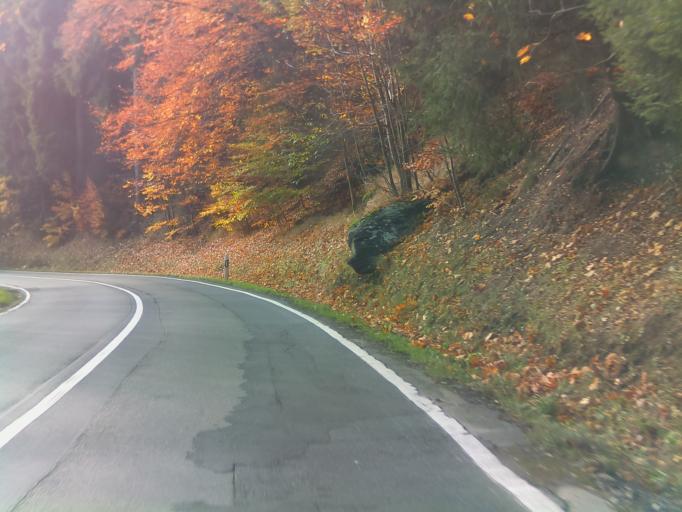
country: DE
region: Thuringia
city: Steinach
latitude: 50.4472
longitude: 11.1449
